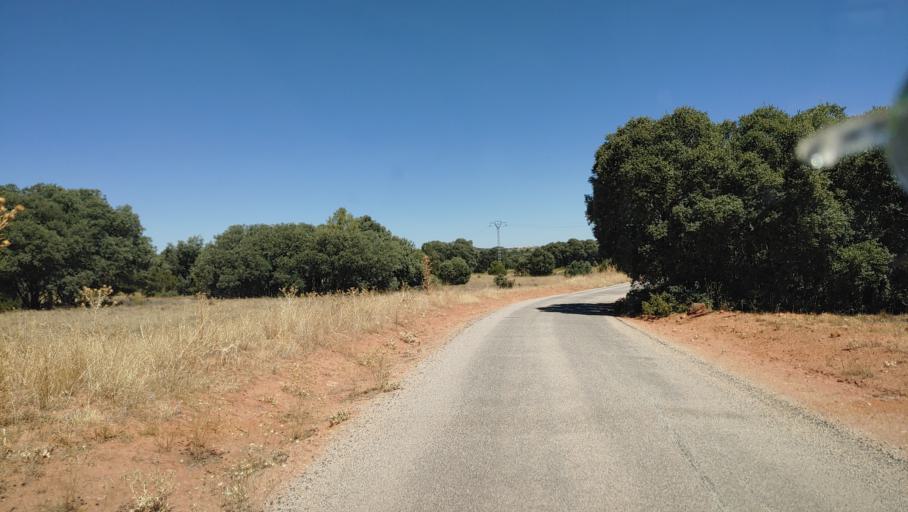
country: ES
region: Castille-La Mancha
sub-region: Provincia de Albacete
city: Ossa de Montiel
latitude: 38.9215
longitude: -2.7937
